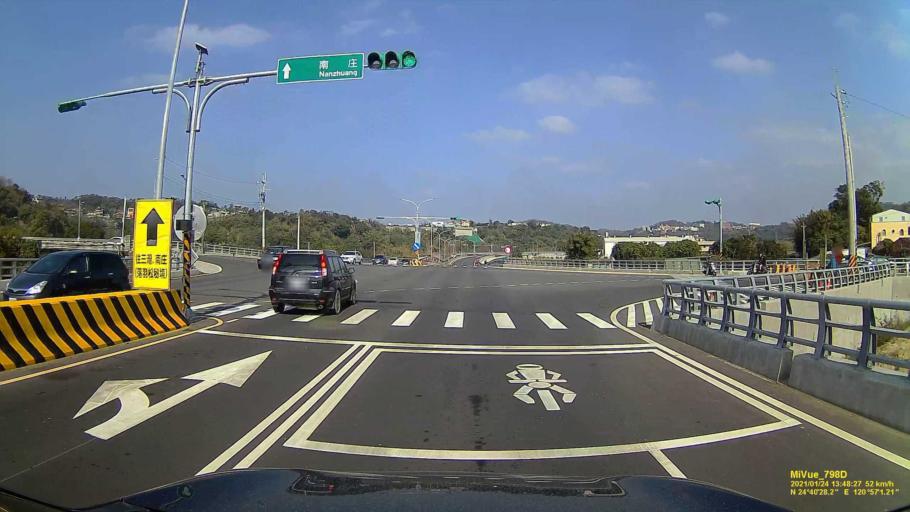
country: TW
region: Taiwan
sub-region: Hsinchu
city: Hsinchu
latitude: 24.6762
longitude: 120.9519
